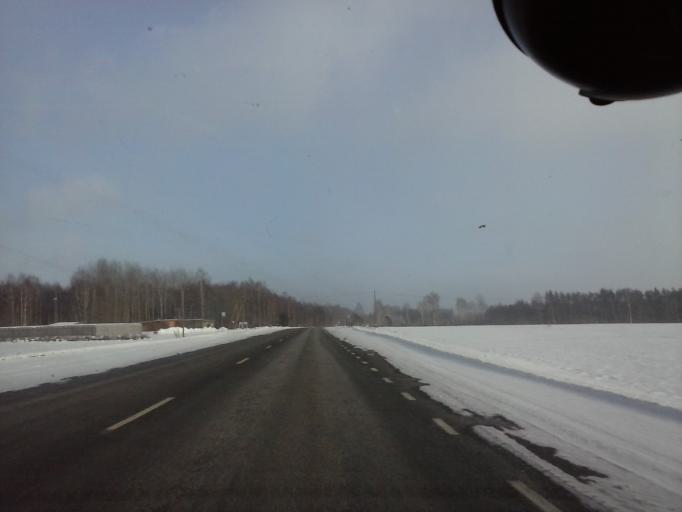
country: EE
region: Tartu
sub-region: Puhja vald
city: Puhja
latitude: 58.3296
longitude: 26.2100
